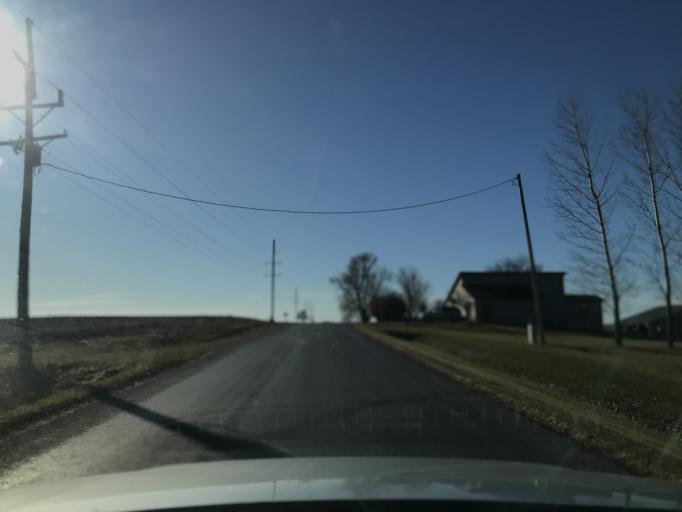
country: US
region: Illinois
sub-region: Hancock County
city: Carthage
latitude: 40.4876
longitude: -91.1780
